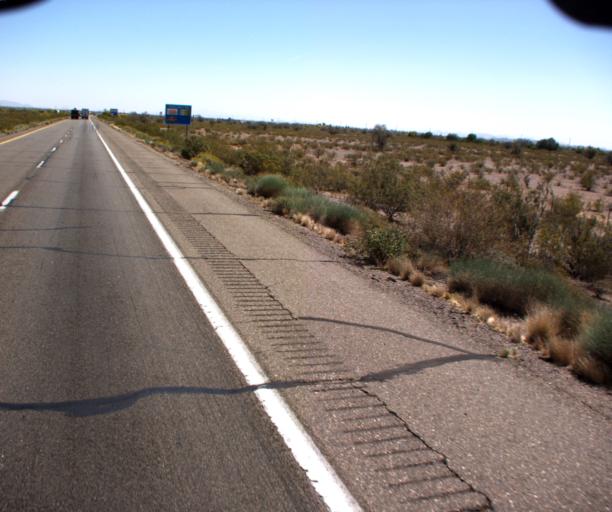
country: US
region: Arizona
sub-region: Maricopa County
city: Buckeye
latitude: 33.5007
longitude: -112.9544
